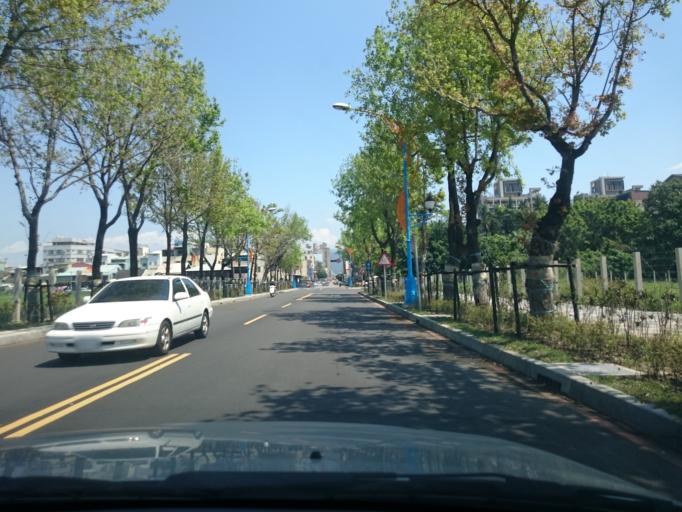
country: TW
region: Taiwan
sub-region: Taichung City
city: Taichung
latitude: 24.1388
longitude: 120.6929
